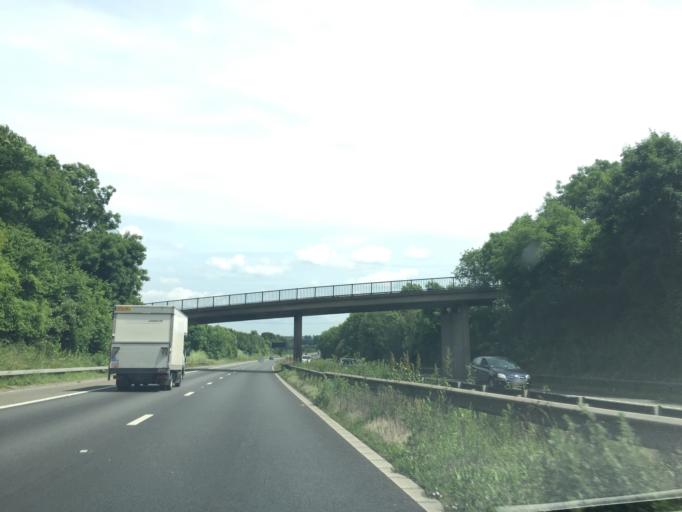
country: GB
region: England
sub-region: Kent
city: Rainham
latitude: 51.3418
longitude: 0.6261
